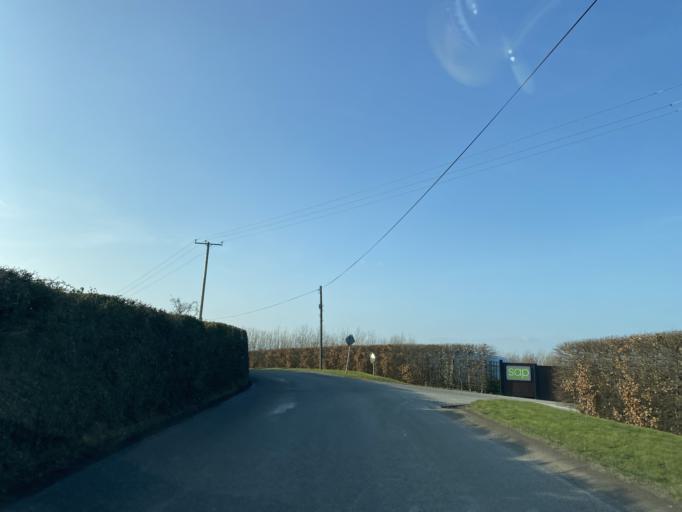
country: IE
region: Leinster
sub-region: Kildare
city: Maynooth
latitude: 53.3627
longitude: -6.5679
